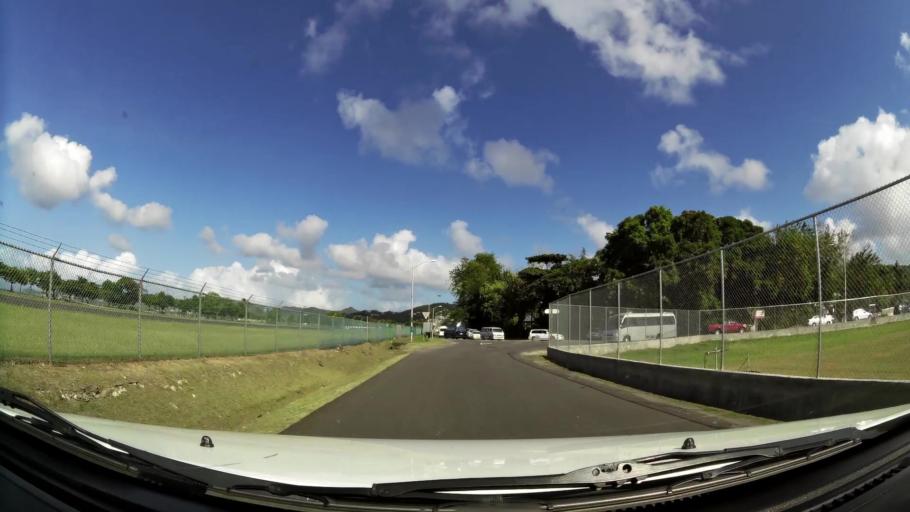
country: LC
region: Castries Quarter
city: Bisee
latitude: 14.0200
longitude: -60.9915
